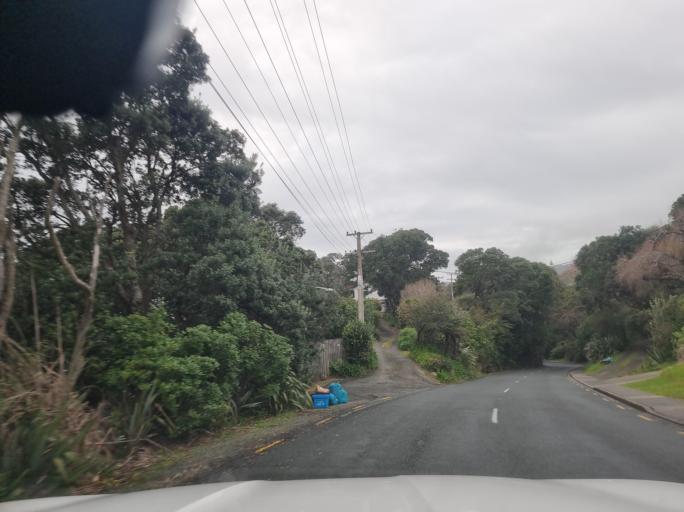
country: NZ
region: Northland
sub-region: Whangarei
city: Ruakaka
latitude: -36.0413
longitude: 174.5290
